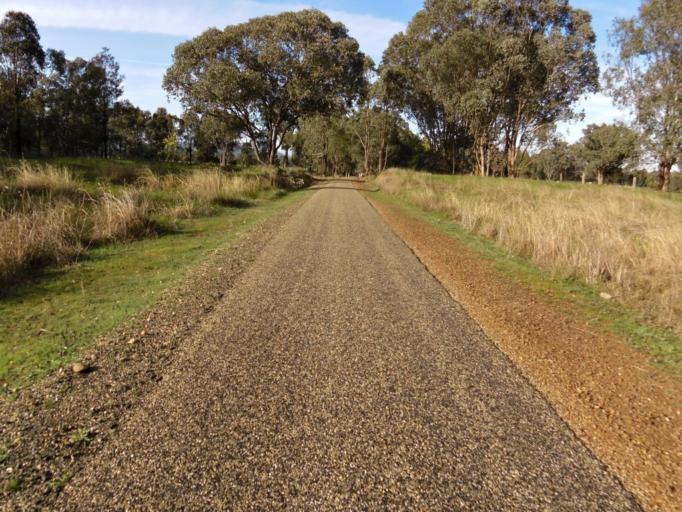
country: AU
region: Victoria
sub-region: Wangaratta
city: Wangaratta
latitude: -36.4134
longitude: 146.5498
